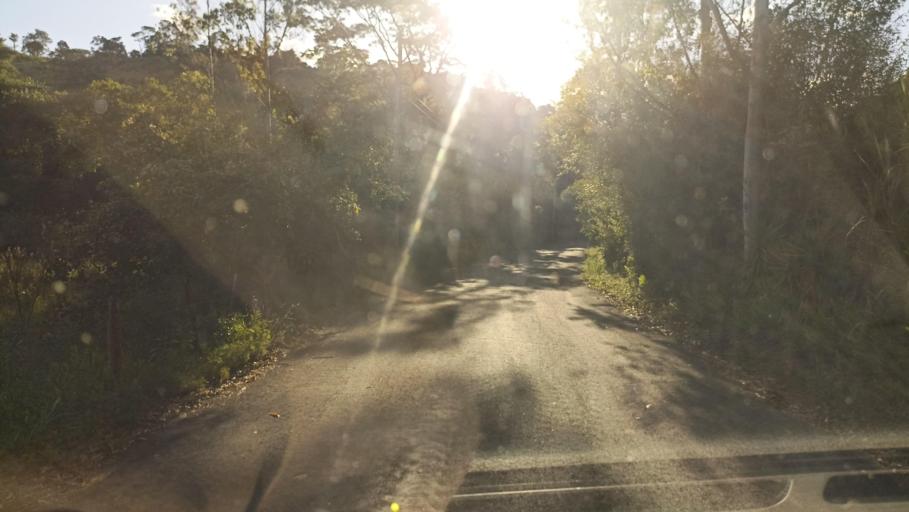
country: BR
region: Minas Gerais
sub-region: Ouro Preto
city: Ouro Preto
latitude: -20.3144
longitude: -43.5915
